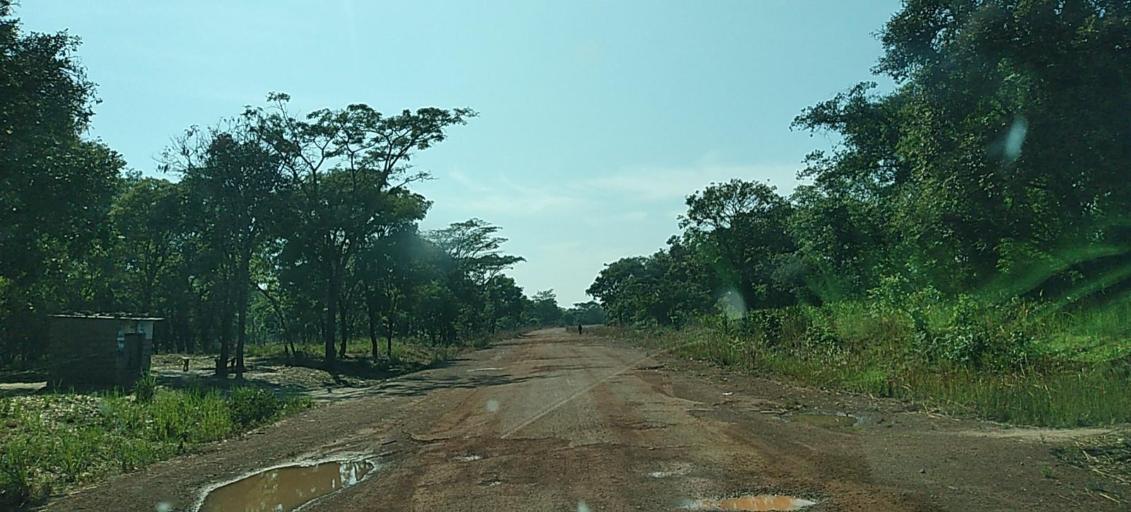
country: ZM
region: North-Western
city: Mwinilunga
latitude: -11.7913
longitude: 25.0673
